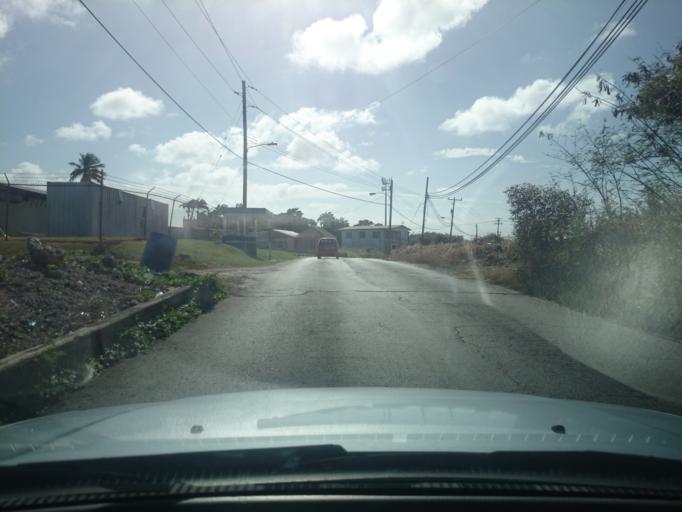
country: BB
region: Saint Lucy
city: Checker Hall
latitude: 13.2946
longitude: -59.6218
